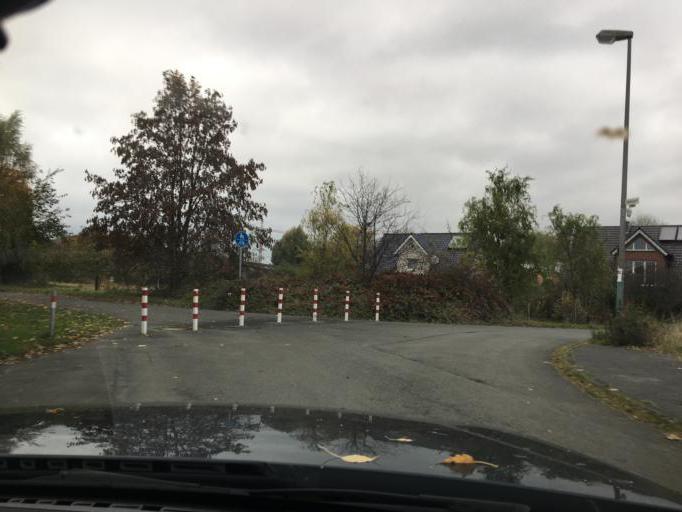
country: DE
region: North Rhine-Westphalia
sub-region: Regierungsbezirk Munster
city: Muenster
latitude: 51.9886
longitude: 7.6535
